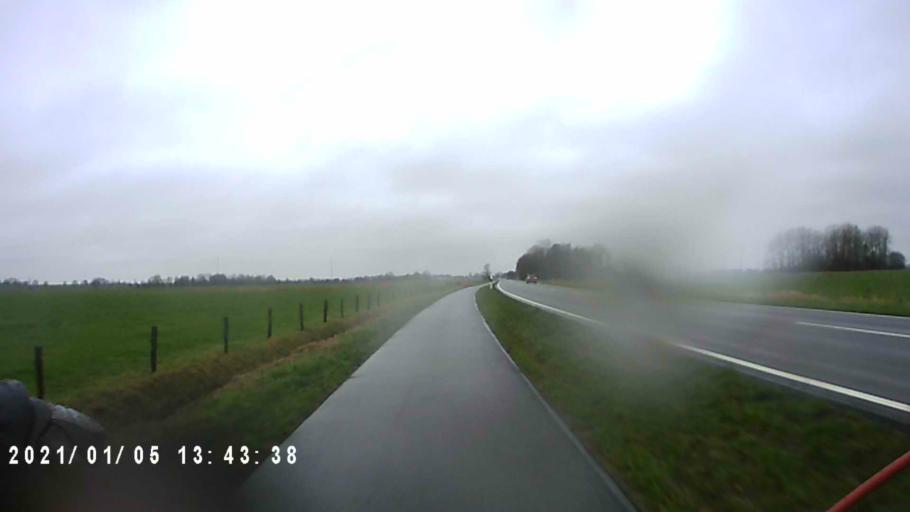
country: DE
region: Lower Saxony
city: Weener
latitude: 53.1951
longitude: 7.3961
